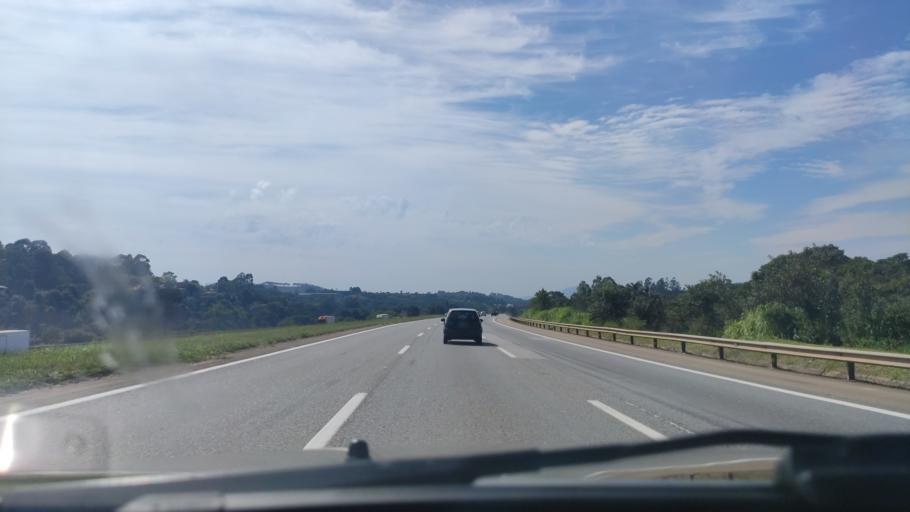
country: BR
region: Sao Paulo
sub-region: Mairinque
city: Mairinque
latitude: -23.4192
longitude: -47.2186
